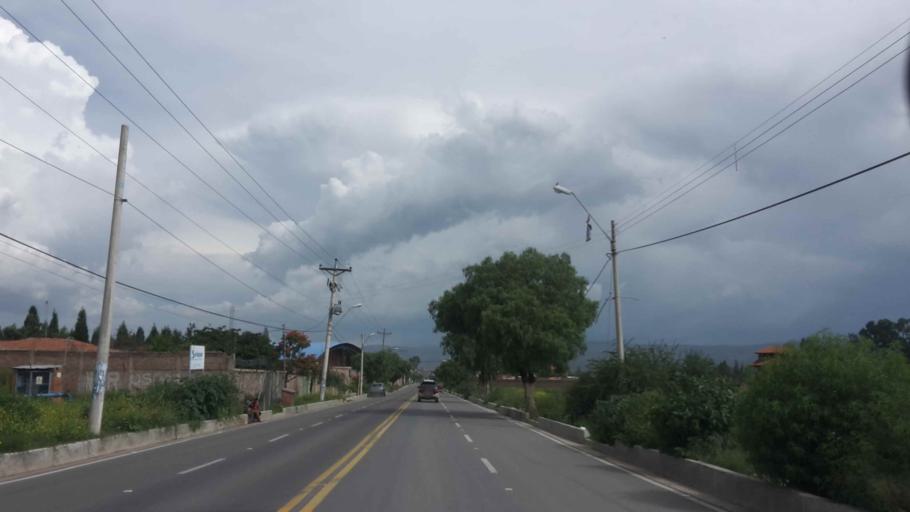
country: BO
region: Cochabamba
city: Cochabamba
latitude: -17.3437
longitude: -66.2603
